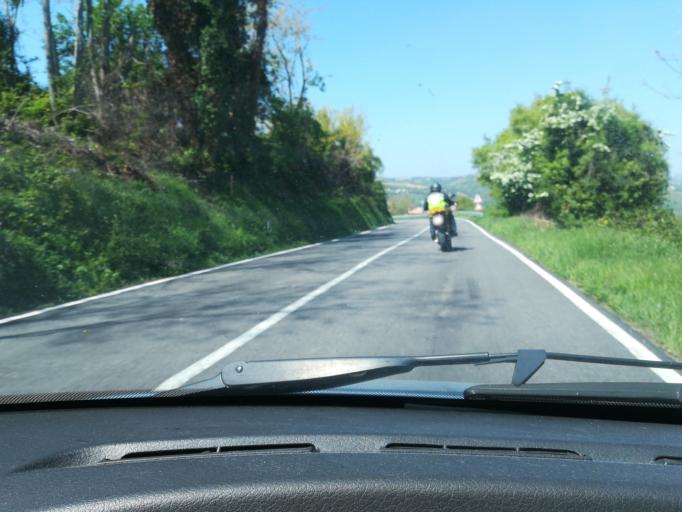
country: IT
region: The Marches
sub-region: Provincia di Macerata
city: Cingoli
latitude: 43.3885
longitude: 13.2052
